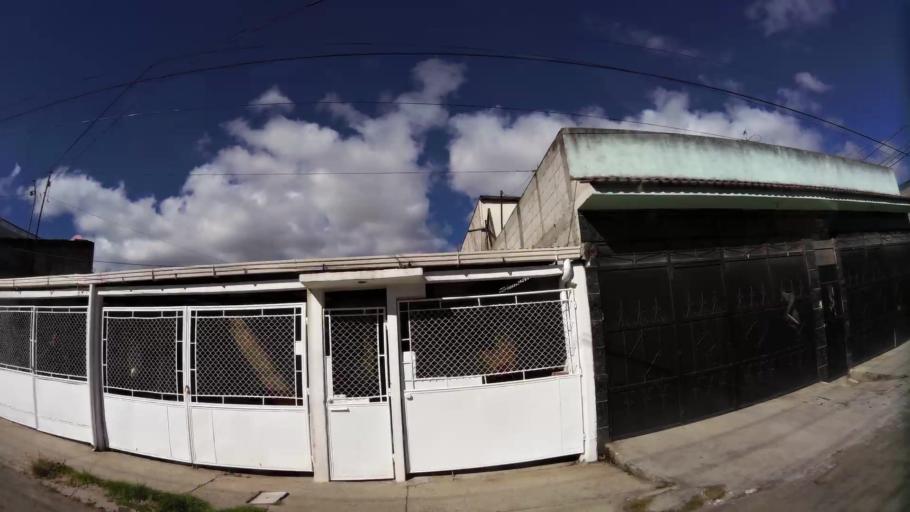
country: GT
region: Quetzaltenango
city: Quetzaltenango
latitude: 14.8371
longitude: -91.5041
